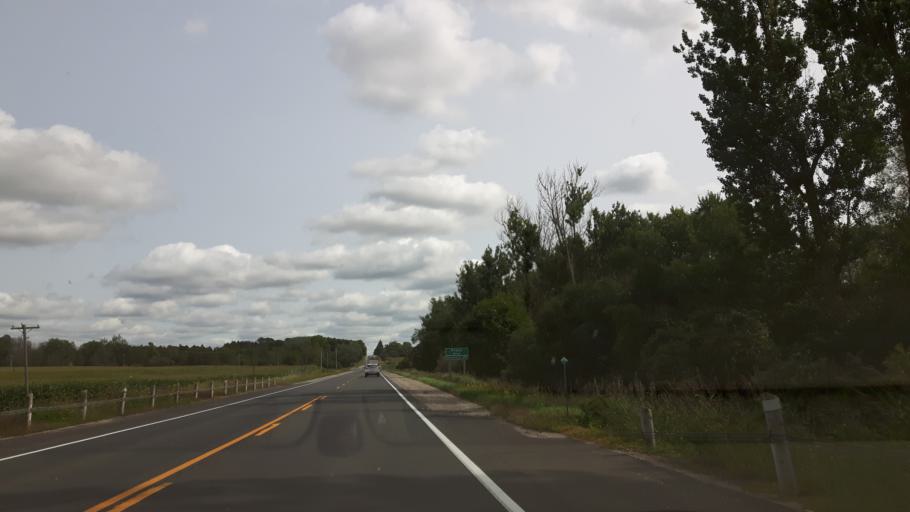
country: CA
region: Ontario
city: Bluewater
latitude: 43.6027
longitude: -81.5065
